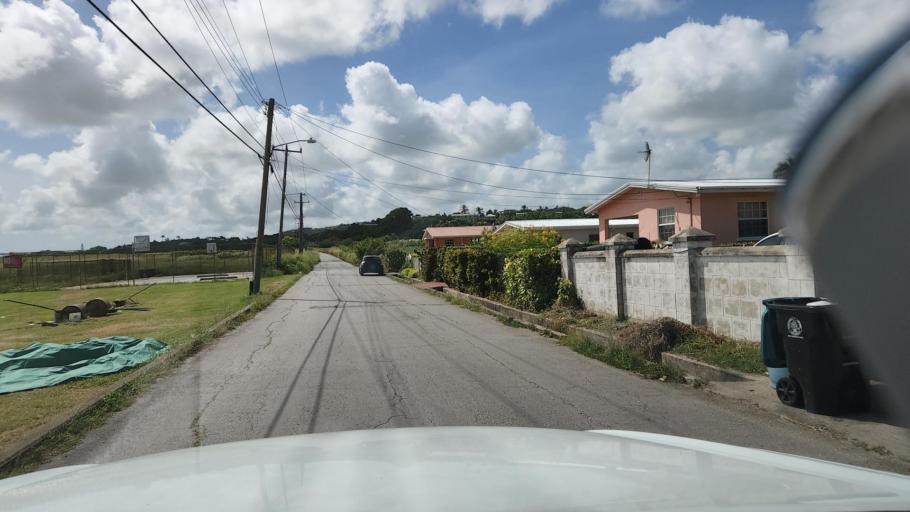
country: BB
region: Saint John
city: Four Cross Roads
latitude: 13.1641
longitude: -59.4547
